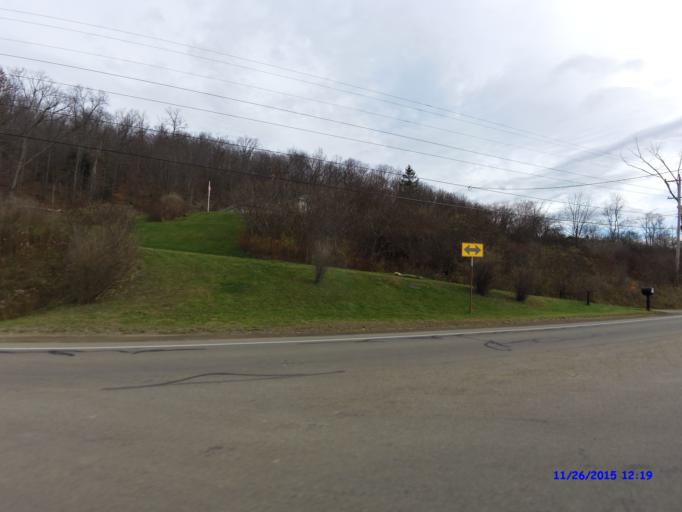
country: US
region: New York
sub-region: Cattaraugus County
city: Saint Bonaventure
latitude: 42.0938
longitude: -78.4674
